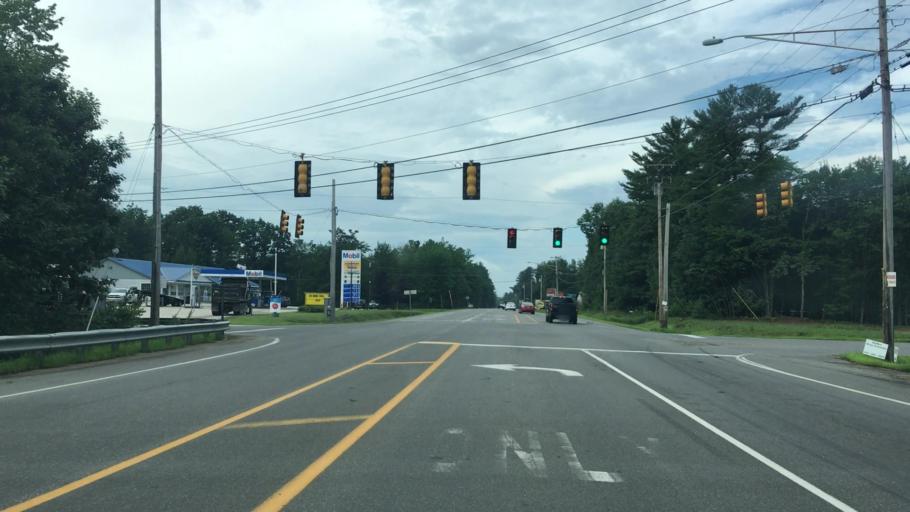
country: US
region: New Hampshire
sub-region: Strafford County
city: Rochester
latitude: 43.3511
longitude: -70.9279
